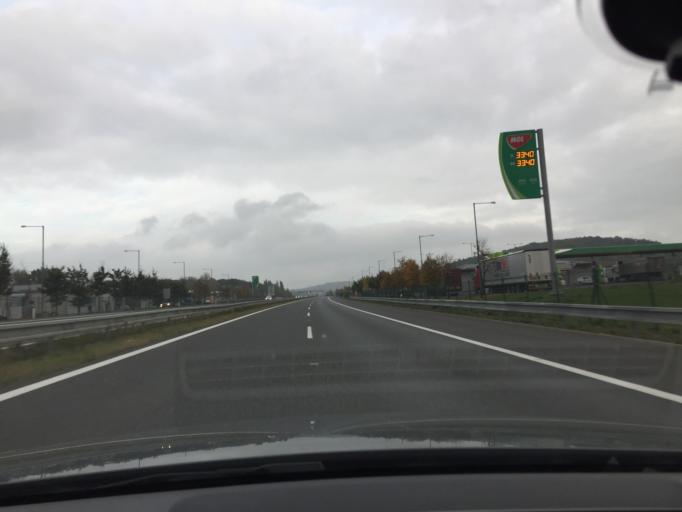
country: CZ
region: Ustecky
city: Chlumec
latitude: 50.7121
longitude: 13.9677
